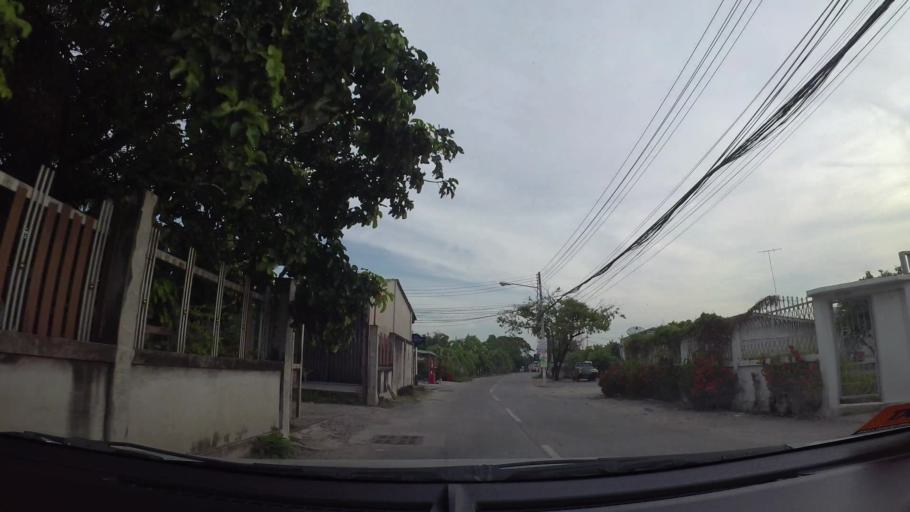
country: TH
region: Chon Buri
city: Chon Buri
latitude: 13.3383
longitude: 100.9806
